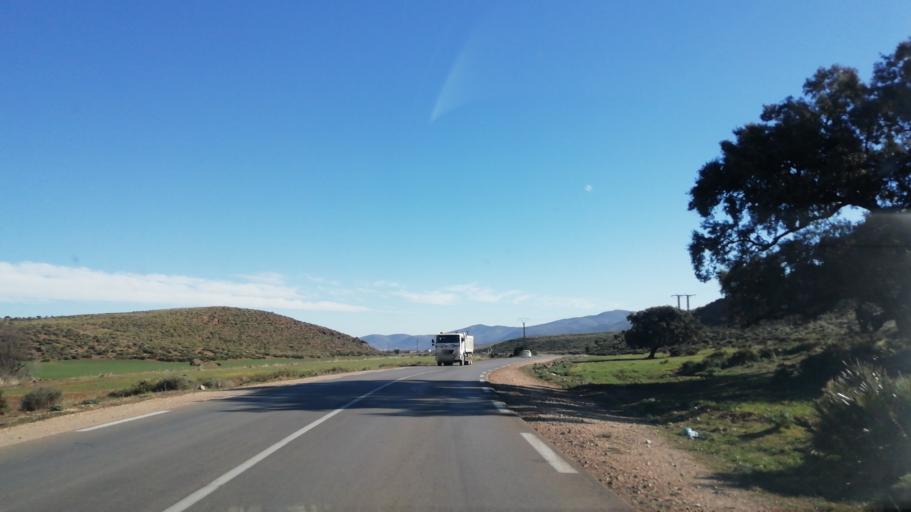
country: DZ
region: Tlemcen
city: Ouled Mimoun
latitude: 34.7726
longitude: -1.1343
